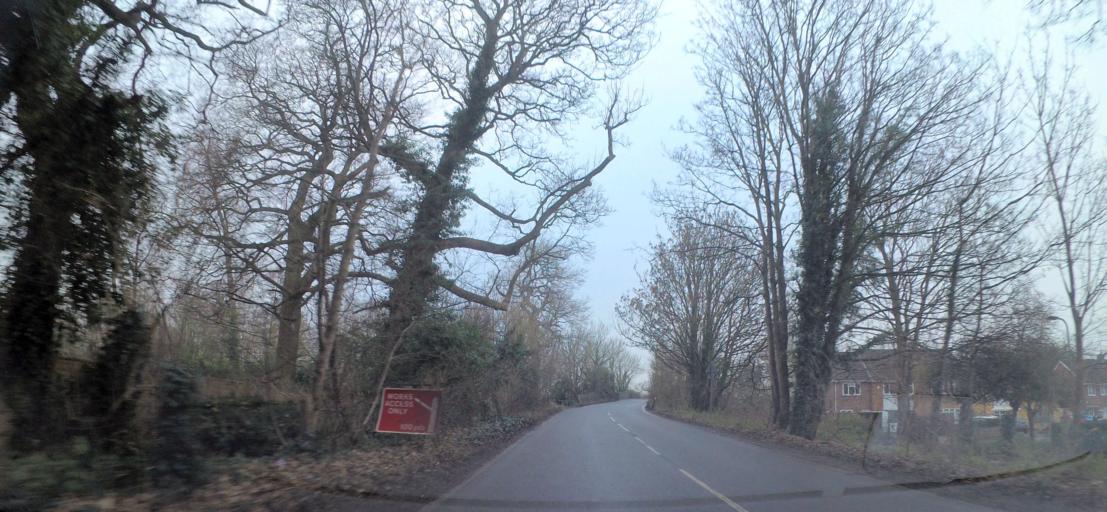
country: GB
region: England
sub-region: West Berkshire
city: Tilehurst
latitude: 51.4382
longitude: -1.0186
